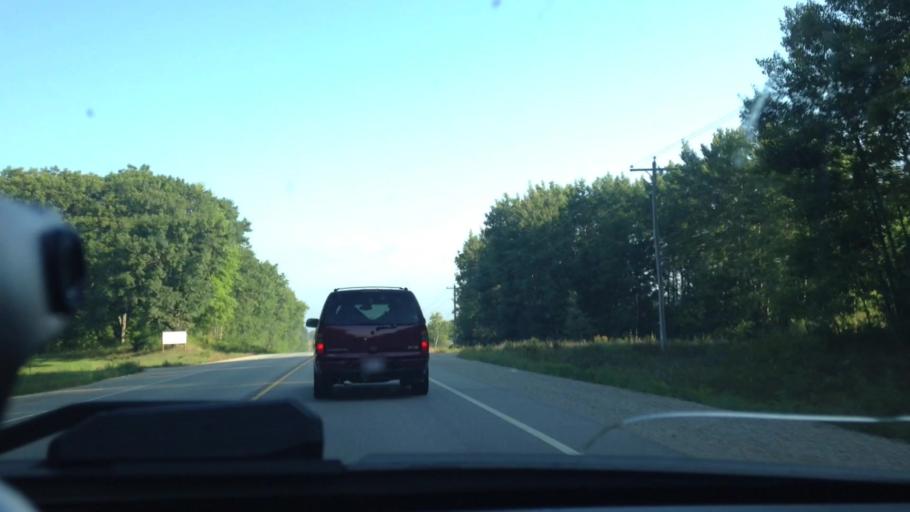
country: US
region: Wisconsin
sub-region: Marinette County
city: Peshtigo
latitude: 45.1725
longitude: -87.9961
